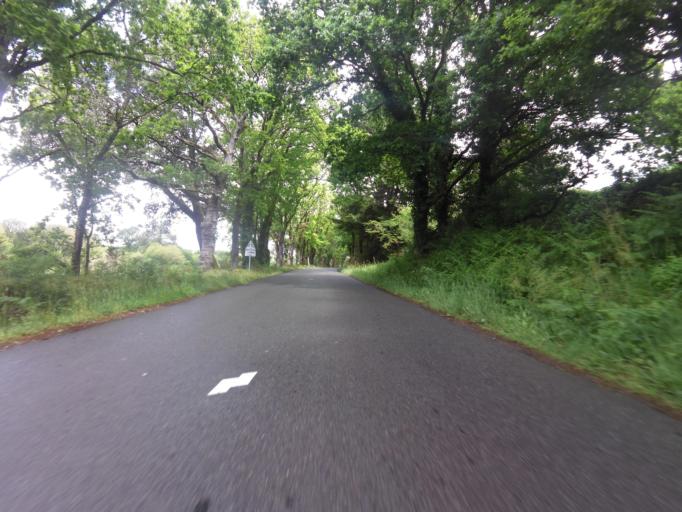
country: FR
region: Brittany
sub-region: Departement du Morbihan
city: Baden
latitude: 47.6095
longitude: -2.9144
